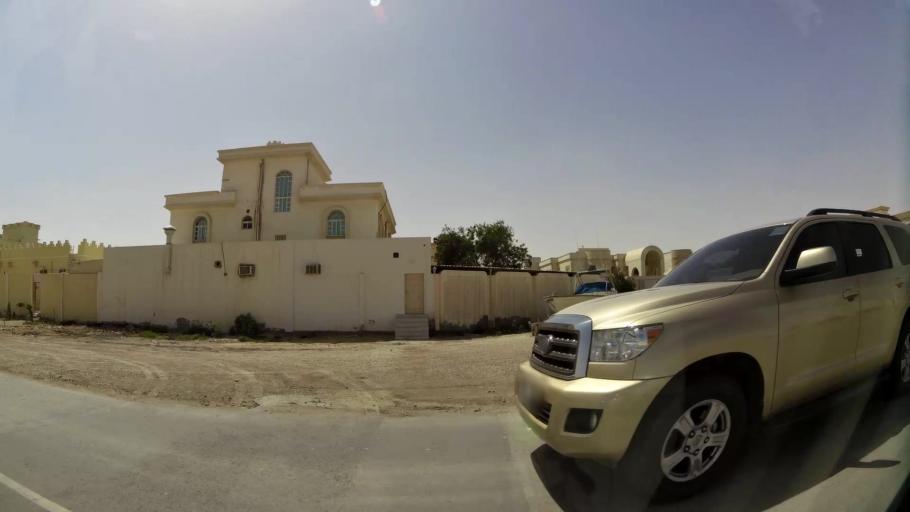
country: QA
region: Baladiyat Umm Salal
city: Umm Salal Muhammad
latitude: 25.3780
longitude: 51.4200
